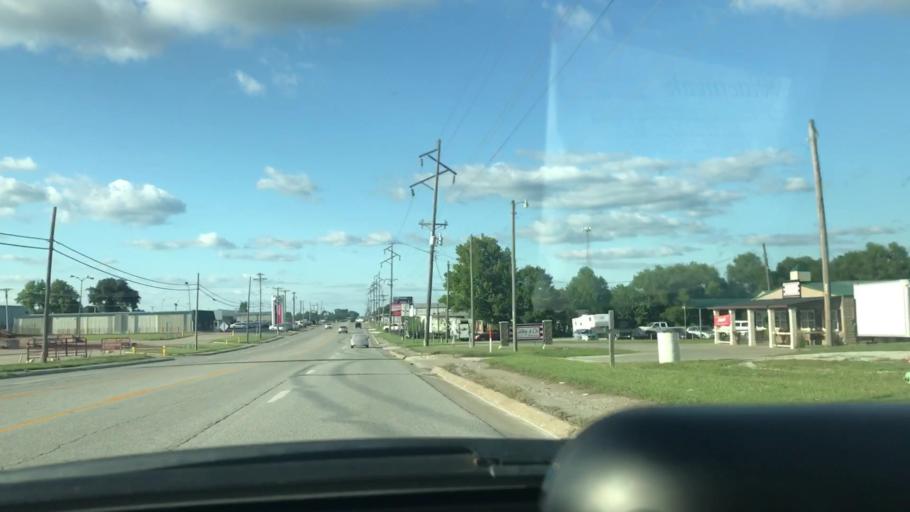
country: US
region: Missouri
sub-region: Pettis County
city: Sedalia
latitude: 38.6776
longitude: -93.2515
